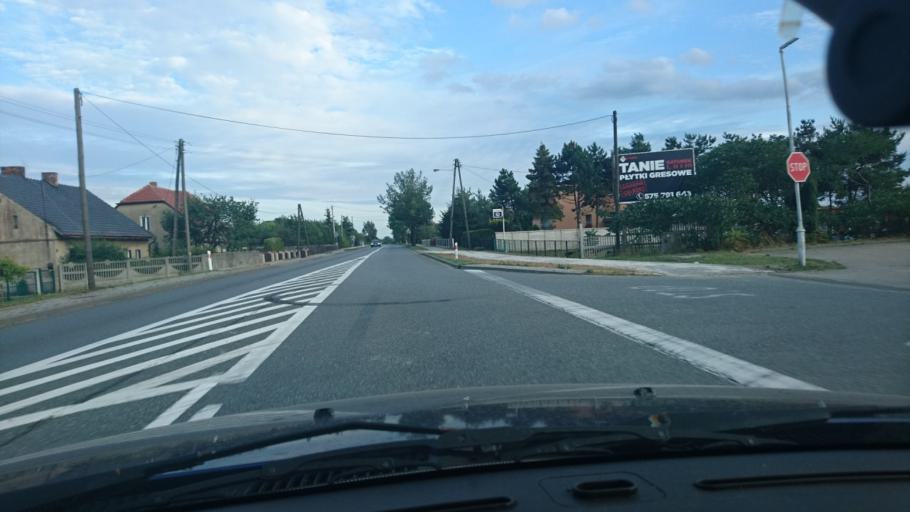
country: PL
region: Opole Voivodeship
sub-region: Powiat oleski
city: Olesno
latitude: 50.8831
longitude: 18.4072
